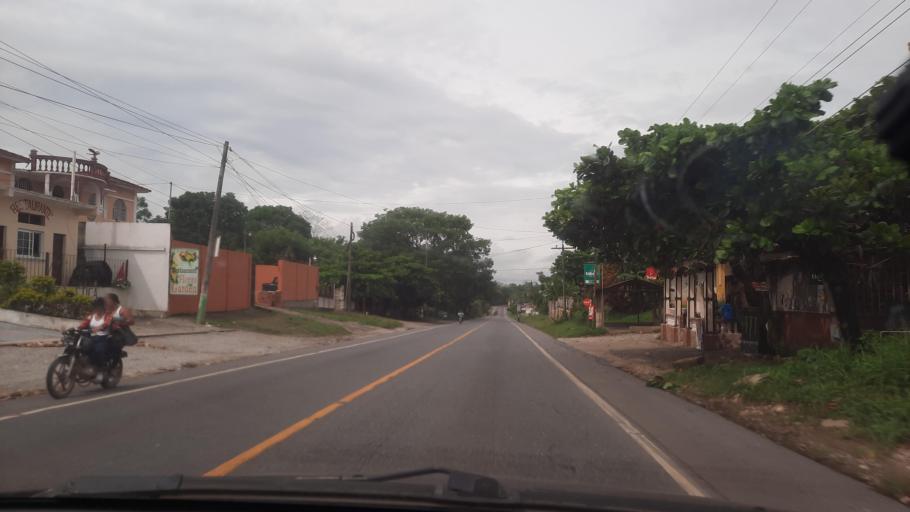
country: GT
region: Izabal
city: Morales
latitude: 15.5200
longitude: -88.7973
